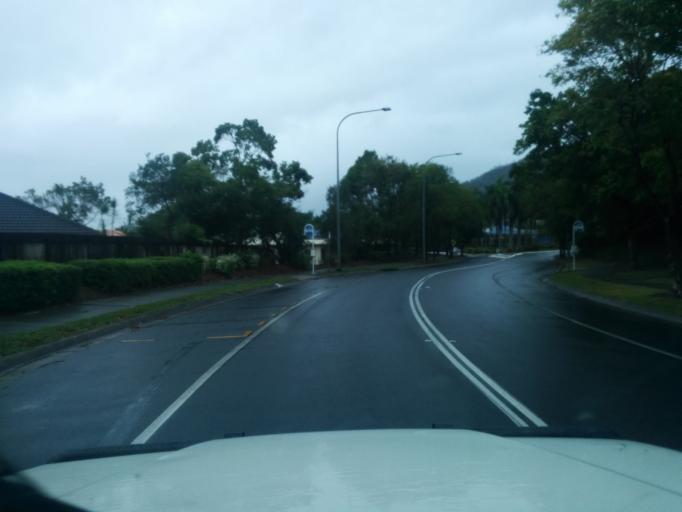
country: AU
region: Queensland
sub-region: Cairns
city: Woree
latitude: -16.9796
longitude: 145.7376
